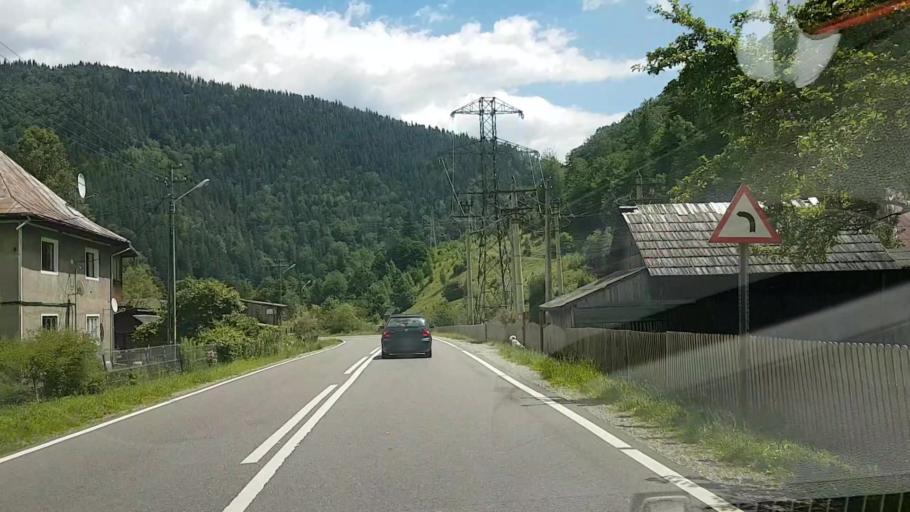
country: RO
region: Suceava
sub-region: Comuna Crucea
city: Crucea
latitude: 47.2826
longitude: 25.6402
